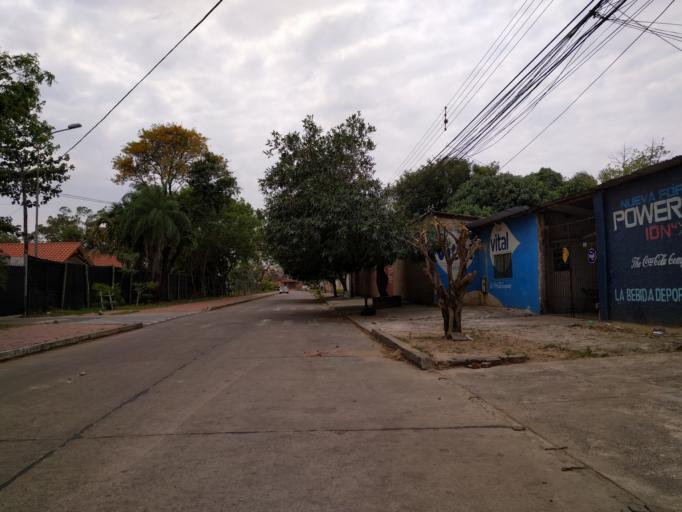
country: BO
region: Santa Cruz
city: Santa Cruz de la Sierra
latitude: -17.7927
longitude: -63.2124
